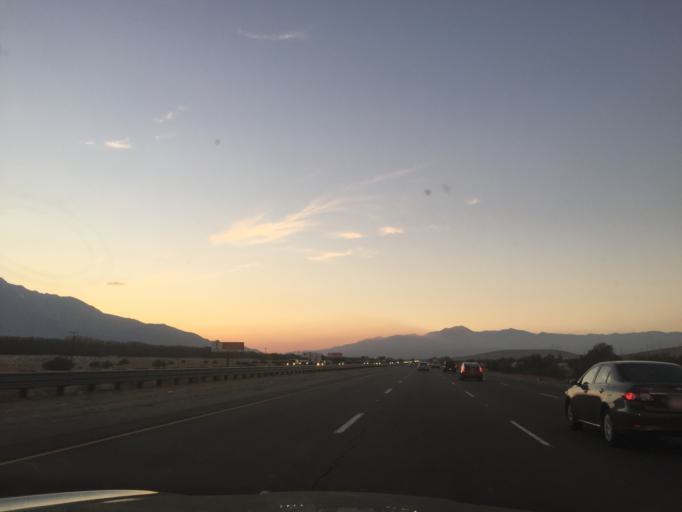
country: US
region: California
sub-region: Riverside County
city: Thousand Palms
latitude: 33.8294
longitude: -116.4245
